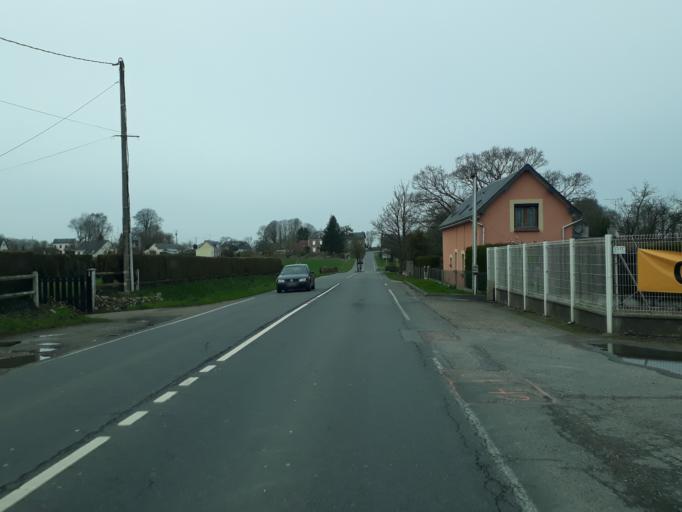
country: FR
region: Haute-Normandie
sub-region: Departement de la Seine-Maritime
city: Beuzeville-la-Grenier
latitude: 49.5939
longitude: 0.4249
